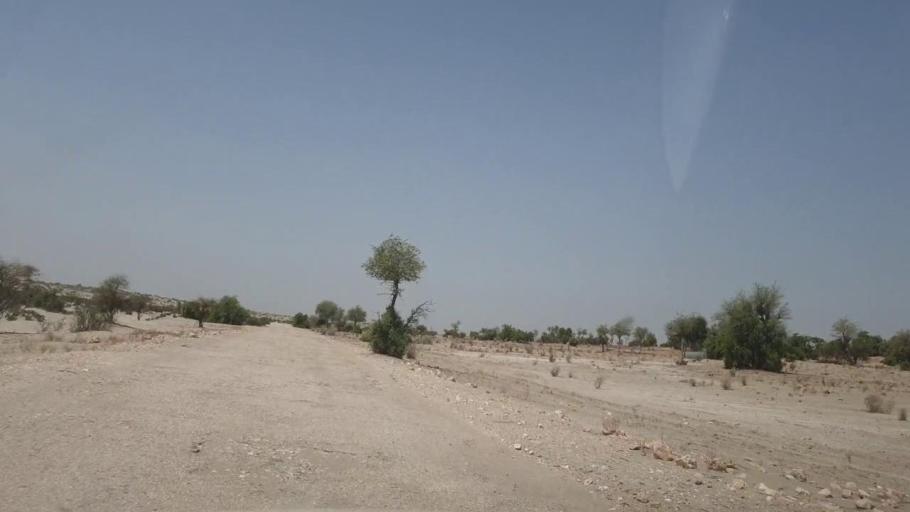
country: PK
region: Sindh
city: Khanpur
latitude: 27.3383
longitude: 69.3137
